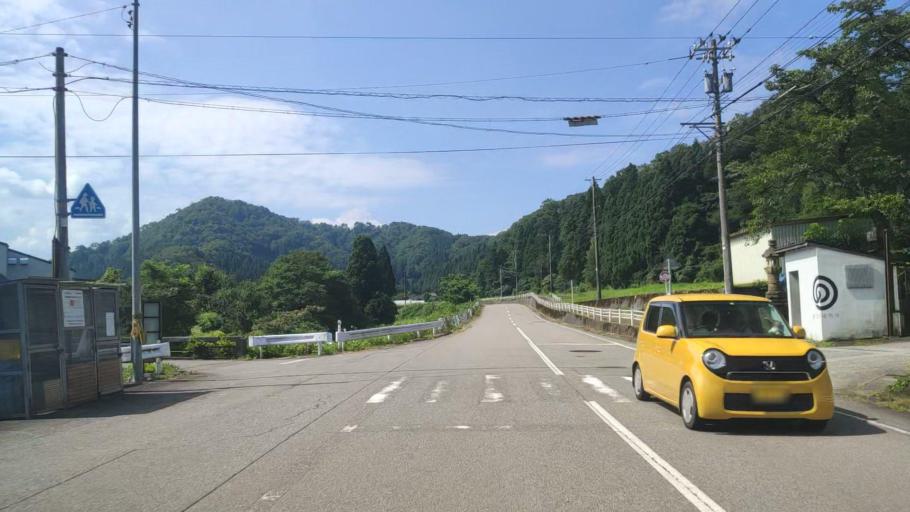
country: JP
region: Ishikawa
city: Komatsu
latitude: 36.3324
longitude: 136.5275
